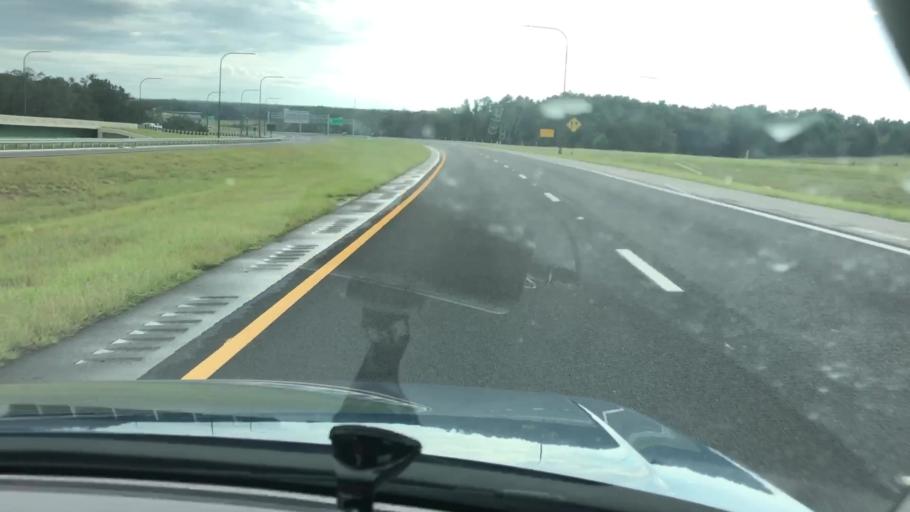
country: US
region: Florida
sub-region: Lake County
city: Mount Plymouth
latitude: 28.7695
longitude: -81.5654
